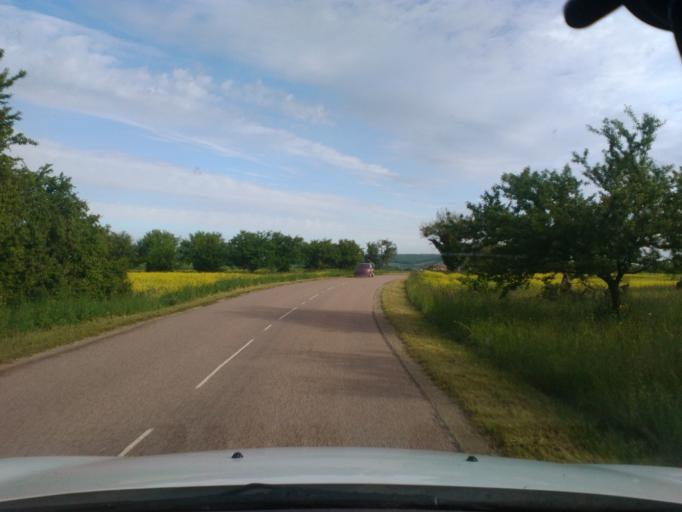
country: FR
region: Lorraine
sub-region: Departement des Vosges
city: Mirecourt
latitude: 48.3145
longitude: 6.1473
